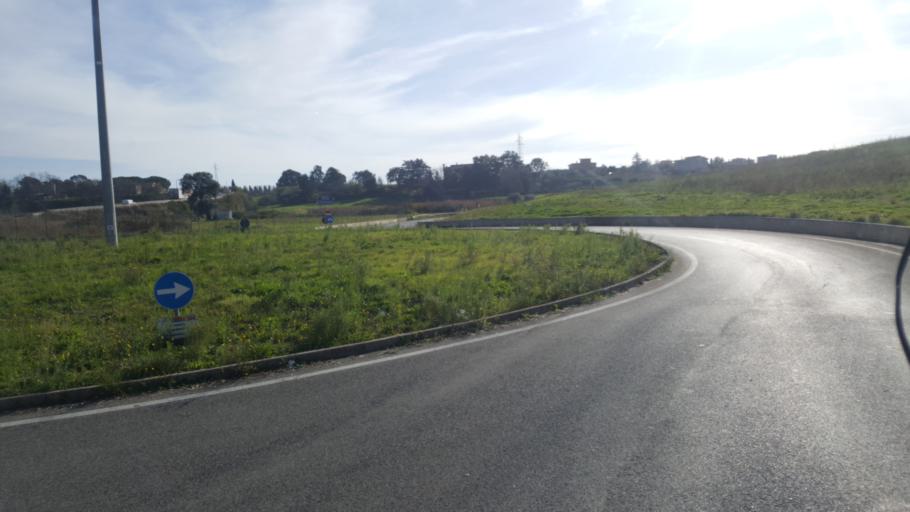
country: IT
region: Latium
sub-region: Citta metropolitana di Roma Capitale
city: Mantiglia di Ardea
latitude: 41.6732
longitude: 12.6326
